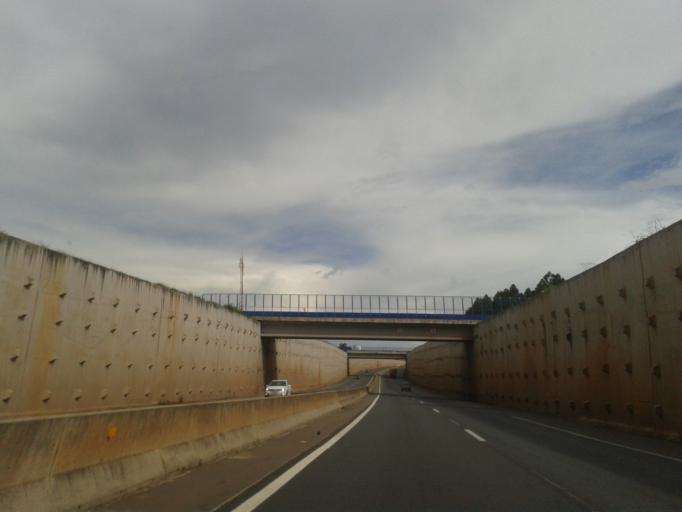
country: BR
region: Goias
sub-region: Hidrolandia
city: Hidrolandia
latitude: -16.9656
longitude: -49.2347
